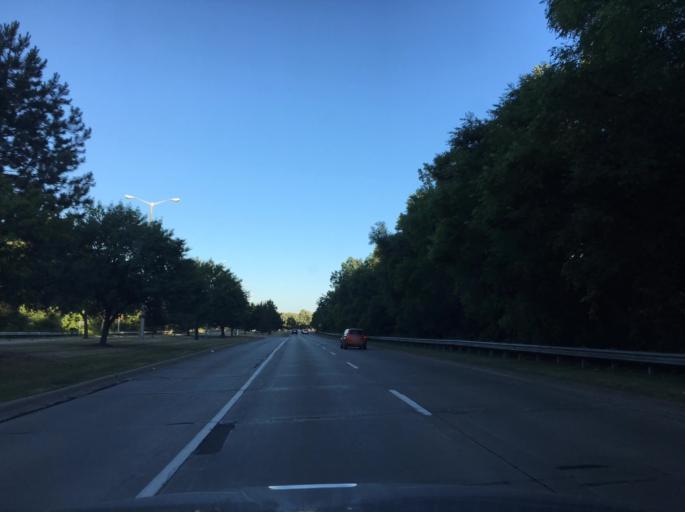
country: US
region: Michigan
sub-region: Macomb County
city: Sterling Heights
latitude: 42.5816
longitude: -82.9924
